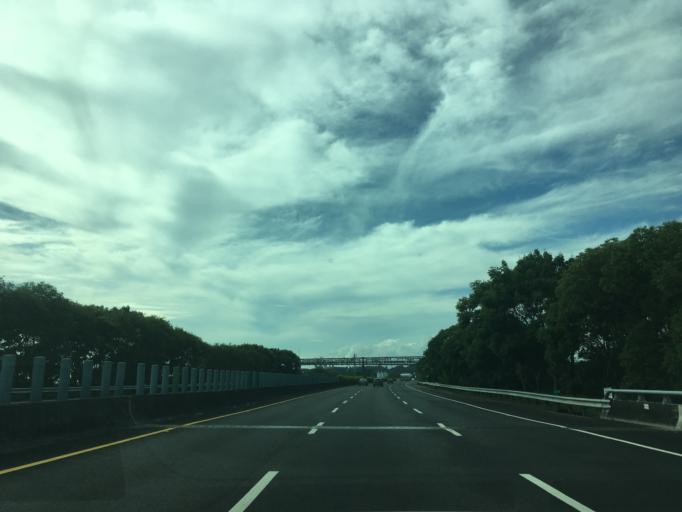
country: TW
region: Taiwan
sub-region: Chiayi
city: Jiayi Shi
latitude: 23.5098
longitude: 120.4873
